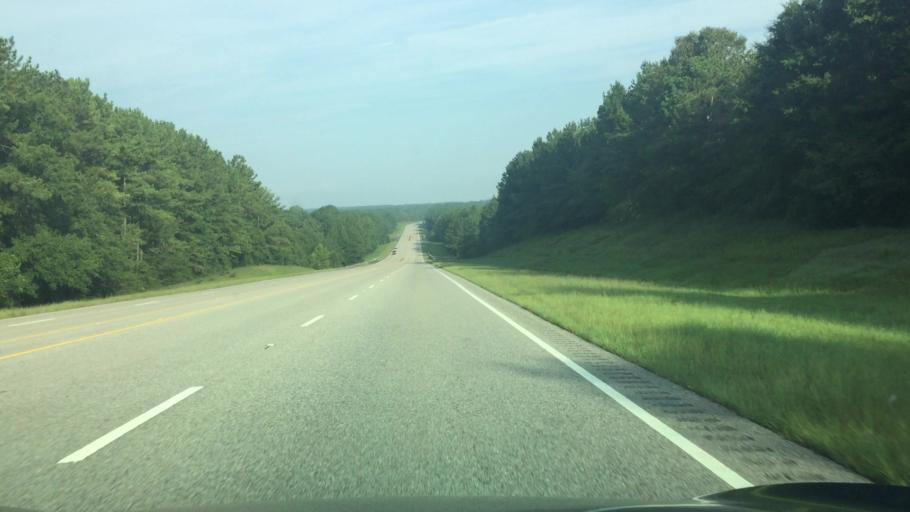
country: US
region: Alabama
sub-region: Butler County
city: Georgiana
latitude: 31.4631
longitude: -86.6491
